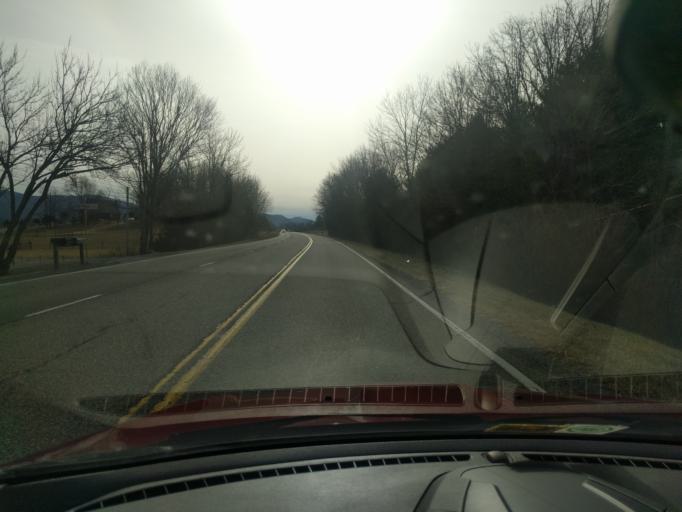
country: US
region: Virginia
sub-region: Augusta County
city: Stuarts Draft
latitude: 37.9540
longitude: -79.1830
